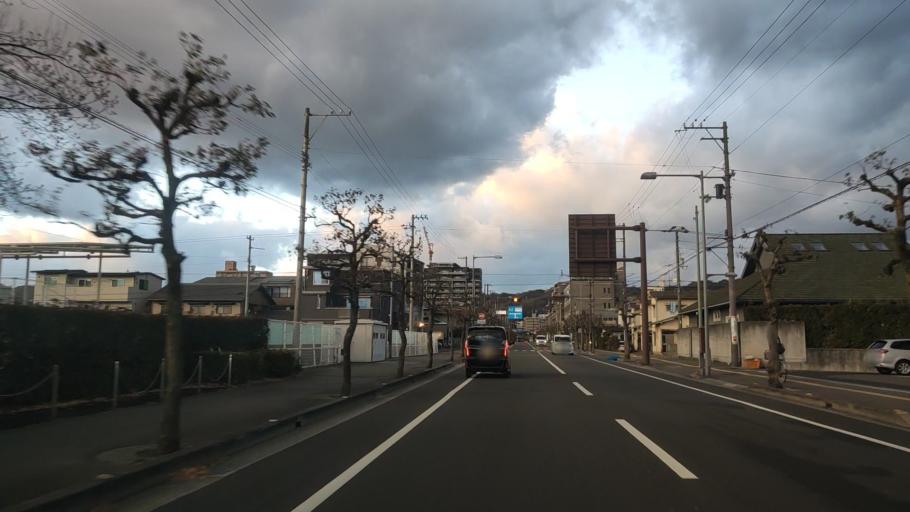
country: JP
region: Ehime
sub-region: Shikoku-chuo Shi
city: Matsuyama
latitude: 33.8436
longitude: 132.7844
